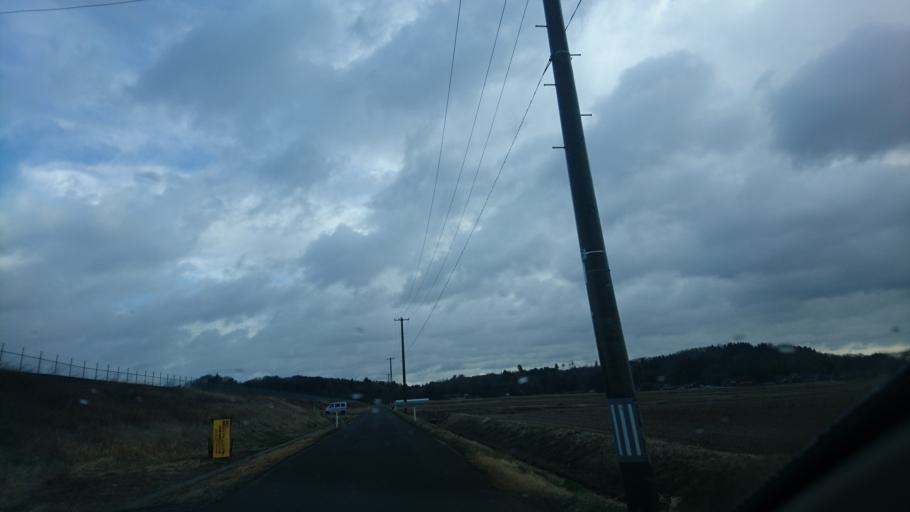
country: JP
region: Iwate
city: Ichinoseki
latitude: 38.7794
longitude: 141.0316
